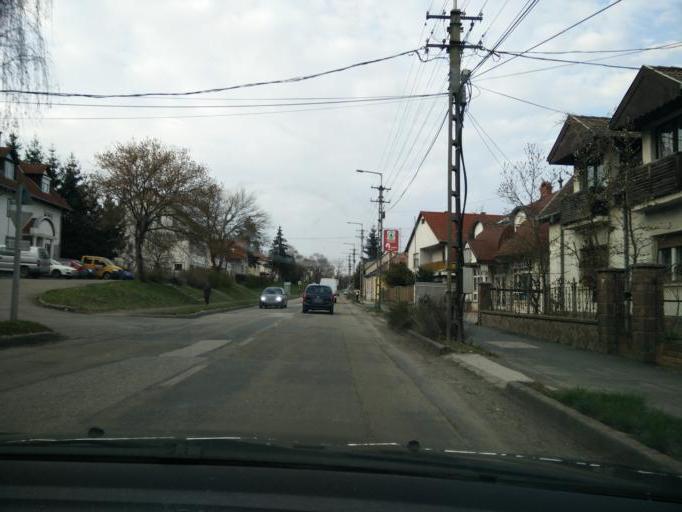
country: HU
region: Zala
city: Zalaegerszeg
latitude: 46.8519
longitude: 16.8451
